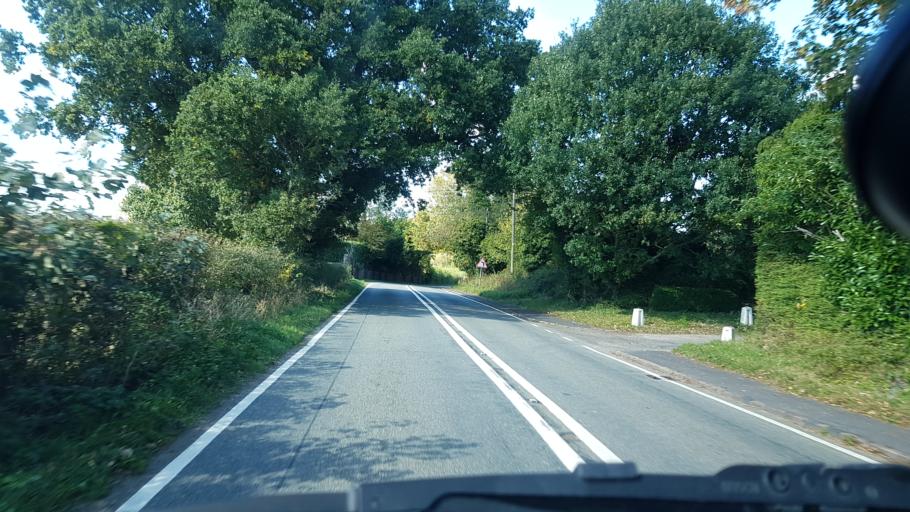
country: GB
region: England
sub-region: West Sussex
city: Billingshurst
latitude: 51.0196
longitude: -0.4972
